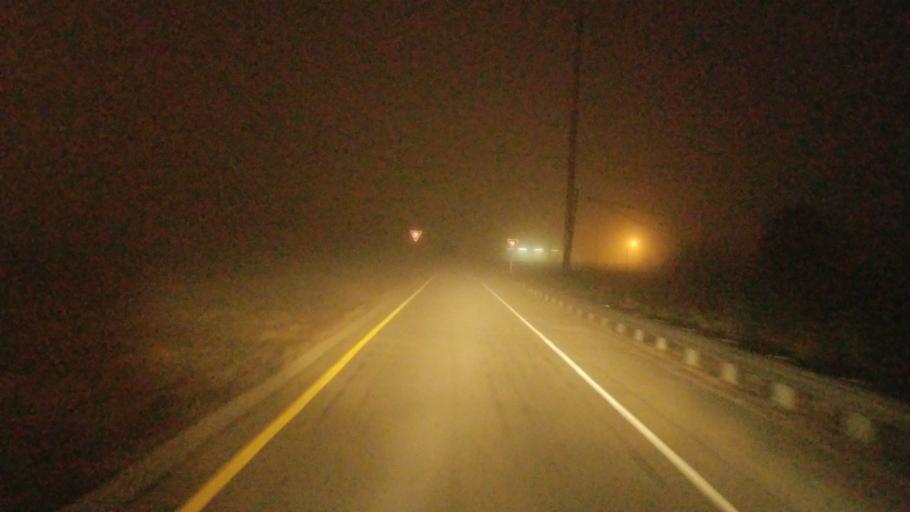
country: US
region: Ohio
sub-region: Scioto County
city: Portsmouth
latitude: 38.7225
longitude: -83.0161
